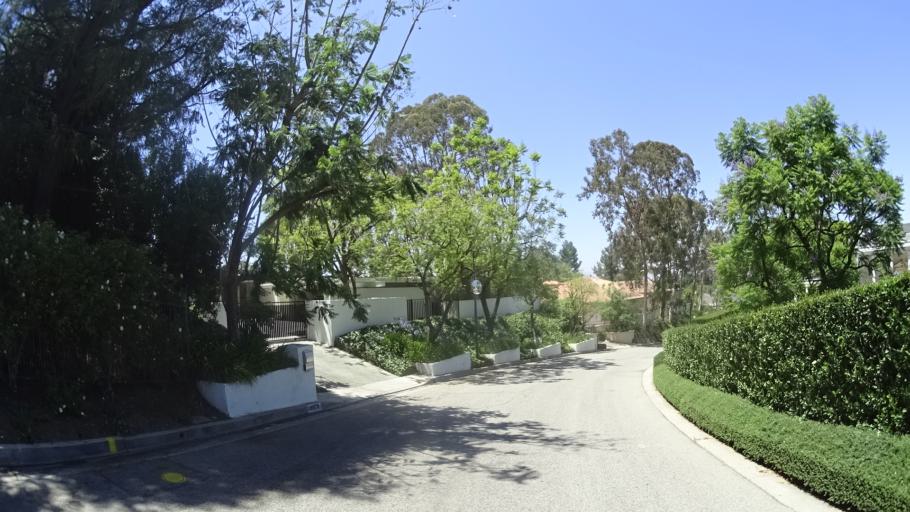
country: US
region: California
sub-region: Los Angeles County
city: Sherman Oaks
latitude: 34.1438
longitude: -118.4844
